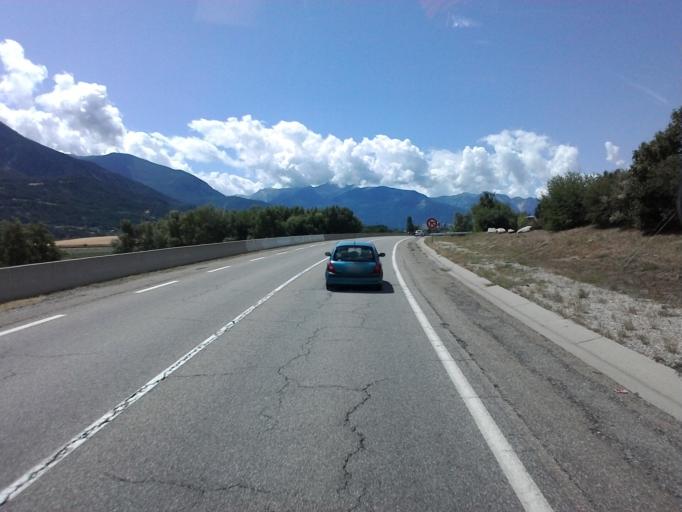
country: FR
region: Provence-Alpes-Cote d'Azur
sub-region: Departement des Hautes-Alpes
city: Embrun
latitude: 44.6164
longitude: 6.5329
